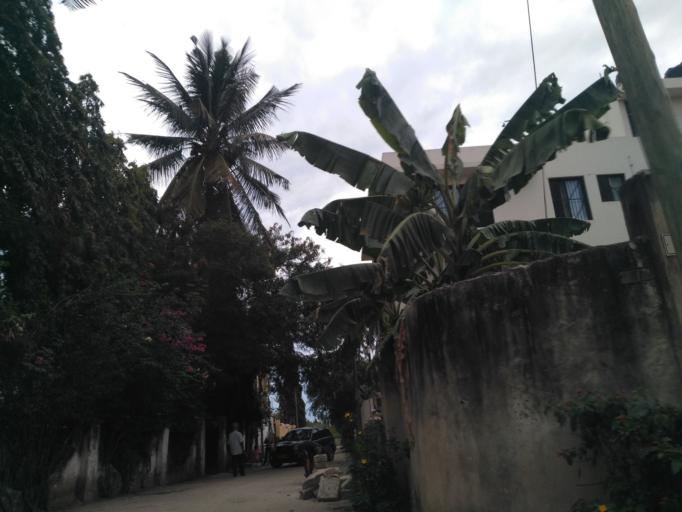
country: TZ
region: Dar es Salaam
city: Magomeni
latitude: -6.7523
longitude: 39.2417
